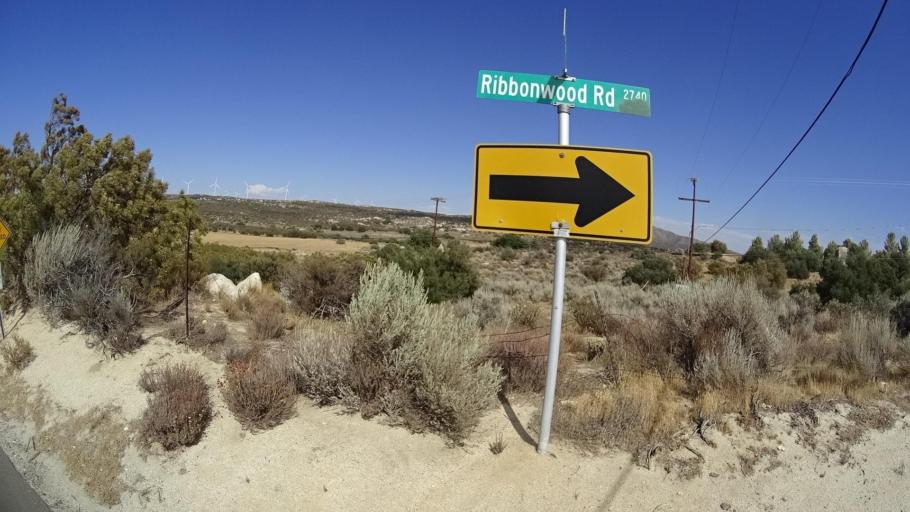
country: US
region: California
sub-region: San Diego County
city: Campo
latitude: 32.6993
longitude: -116.2933
